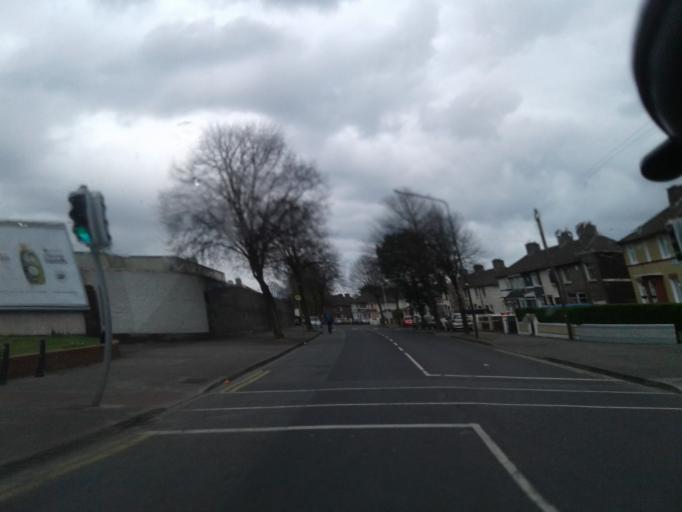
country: IE
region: Leinster
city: Rialto
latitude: 53.3269
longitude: -6.2903
